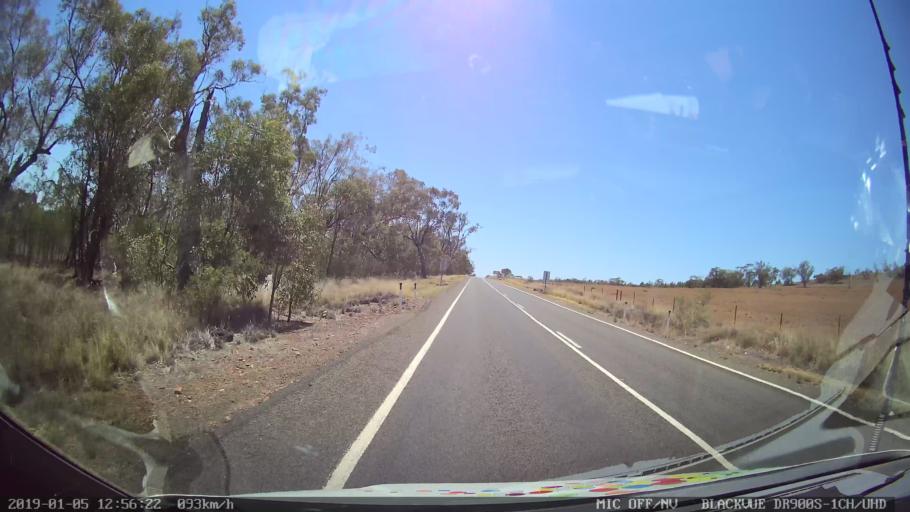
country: AU
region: New South Wales
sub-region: Warrumbungle Shire
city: Coonabarabran
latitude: -31.1148
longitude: 149.7190
